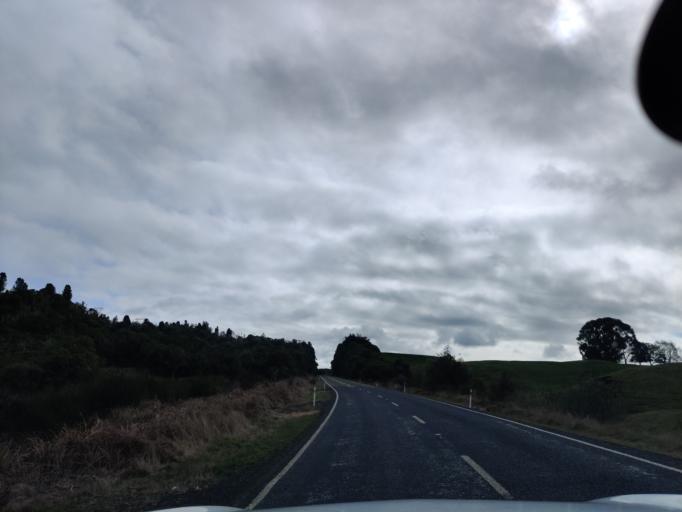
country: NZ
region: Waikato
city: Turangi
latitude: -38.7892
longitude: 175.6886
